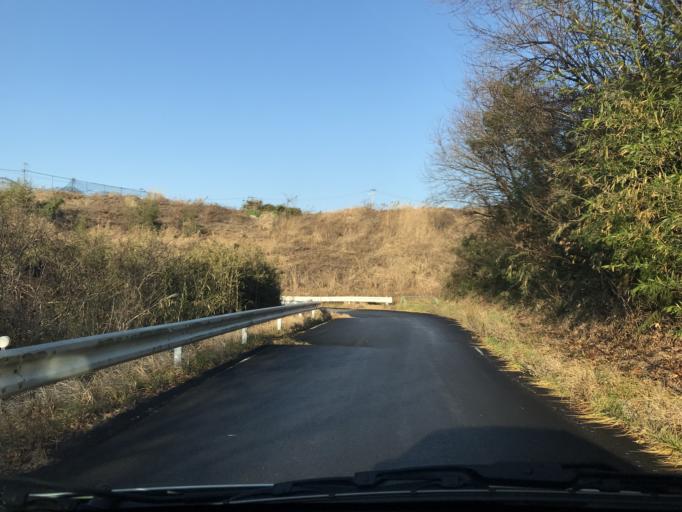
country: JP
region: Miyagi
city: Wakuya
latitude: 38.6937
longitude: 141.1139
